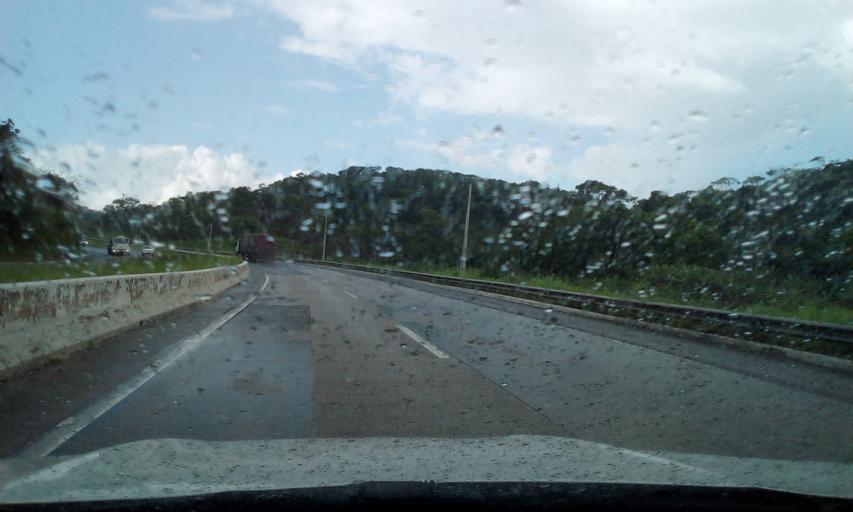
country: BR
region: Pernambuco
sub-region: Cabo De Santo Agostinho
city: Cabo
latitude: -8.3208
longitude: -35.1118
